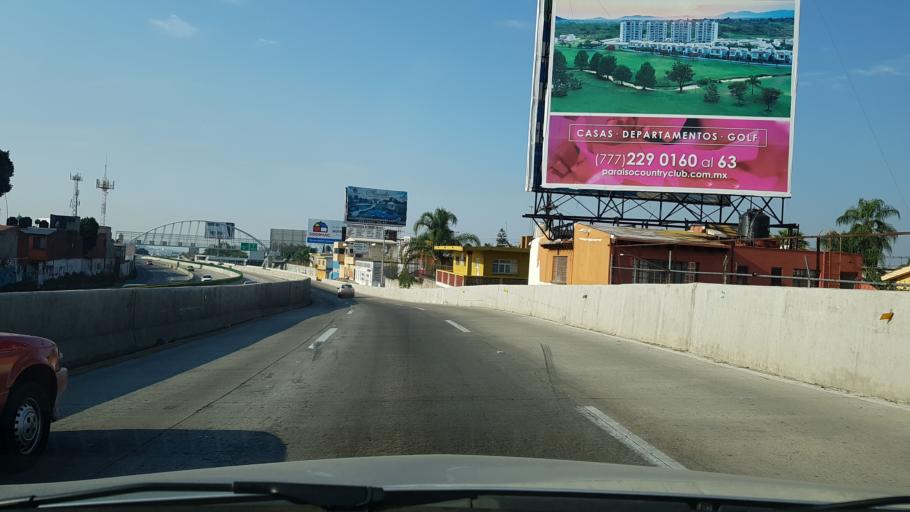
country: MX
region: Morelos
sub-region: Tepoztlan
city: Loma Bonita
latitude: 18.9269
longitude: -99.2026
